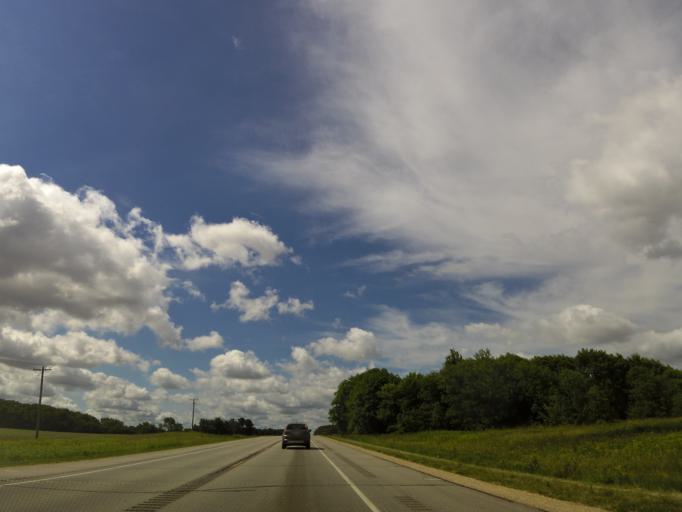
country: US
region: Minnesota
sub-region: Mower County
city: Grand Meadow
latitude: 43.7322
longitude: -92.4793
